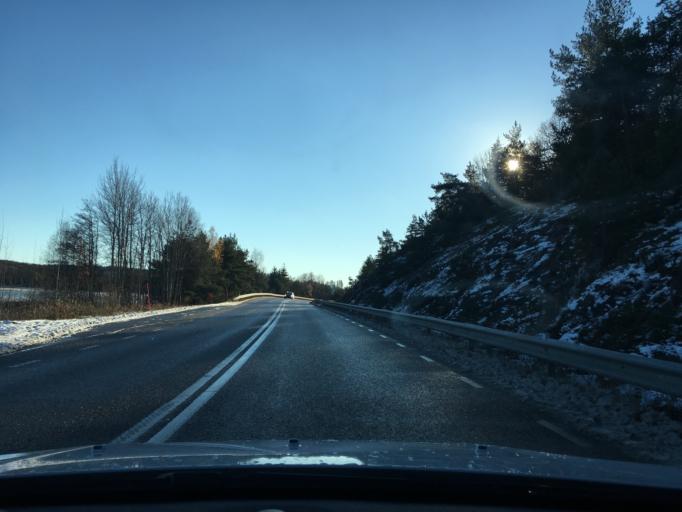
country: SE
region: Vaestra Goetaland
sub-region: Tjorns Kommun
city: Myggenas
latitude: 58.0749
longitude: 11.6961
